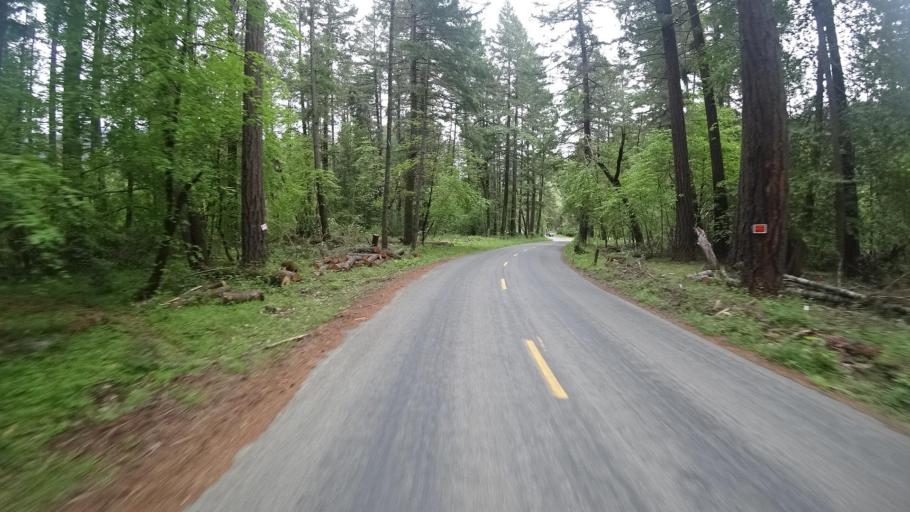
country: US
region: California
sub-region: Humboldt County
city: Willow Creek
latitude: 40.9628
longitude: -123.6320
